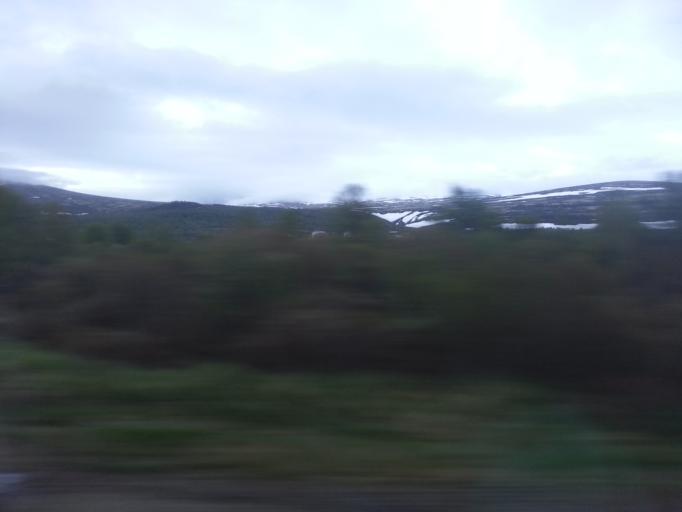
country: NO
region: Oppland
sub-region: Dovre
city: Dovre
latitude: 62.1174
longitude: 9.2739
